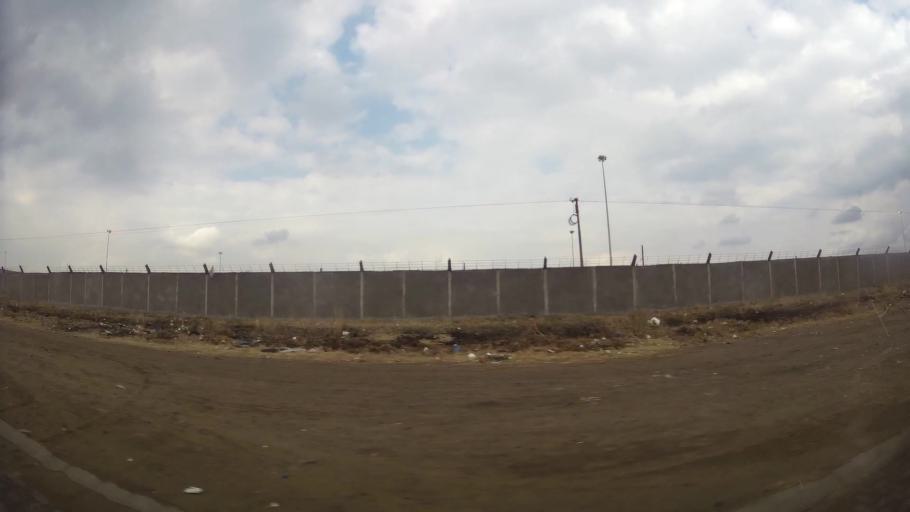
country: ZA
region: Orange Free State
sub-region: Fezile Dabi District Municipality
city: Sasolburg
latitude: -26.8538
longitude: 27.8643
